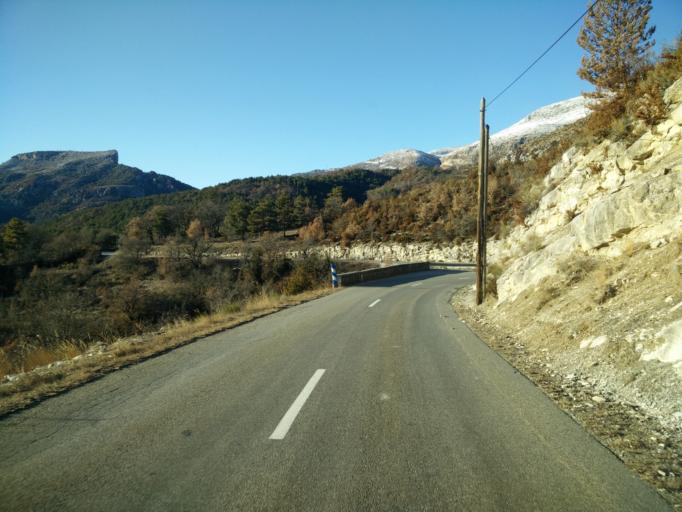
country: FR
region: Provence-Alpes-Cote d'Azur
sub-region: Departement des Alpes-de-Haute-Provence
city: Castellane
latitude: 43.7943
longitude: 6.3894
